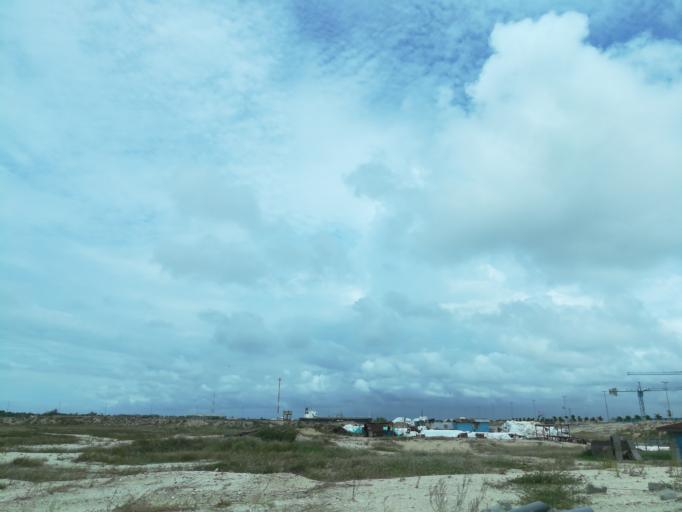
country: NG
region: Lagos
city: Lagos
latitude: 6.4084
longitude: 3.4083
